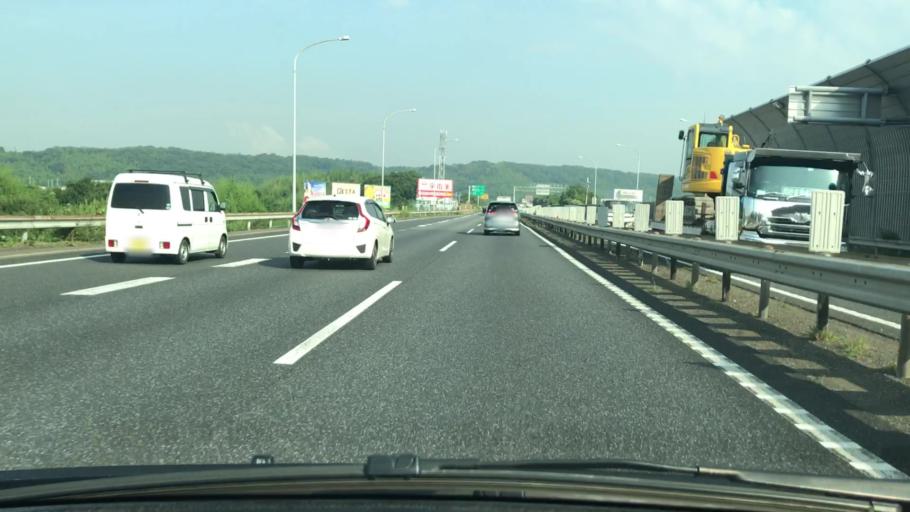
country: JP
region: Hyogo
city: Akashi
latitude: 34.6853
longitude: 134.9793
